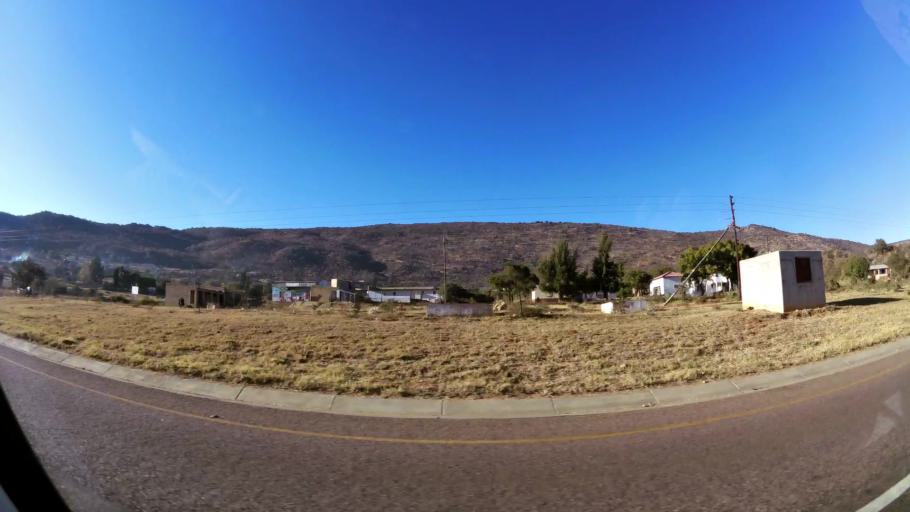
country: ZA
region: Limpopo
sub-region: Capricorn District Municipality
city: Mankoeng
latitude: -23.9412
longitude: 29.8244
